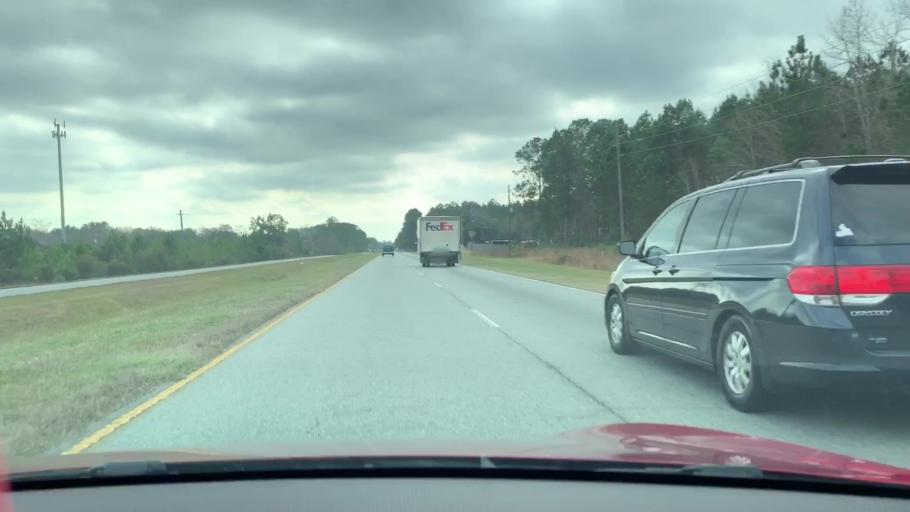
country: US
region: South Carolina
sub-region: Jasper County
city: Hardeeville
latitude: 32.2287
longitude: -81.0744
